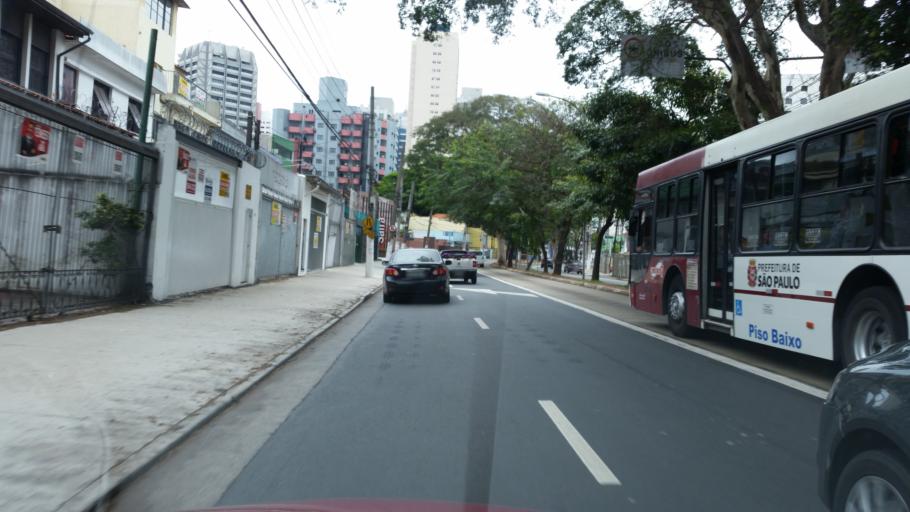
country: BR
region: Sao Paulo
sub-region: Diadema
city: Diadema
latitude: -23.6419
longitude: -46.6993
